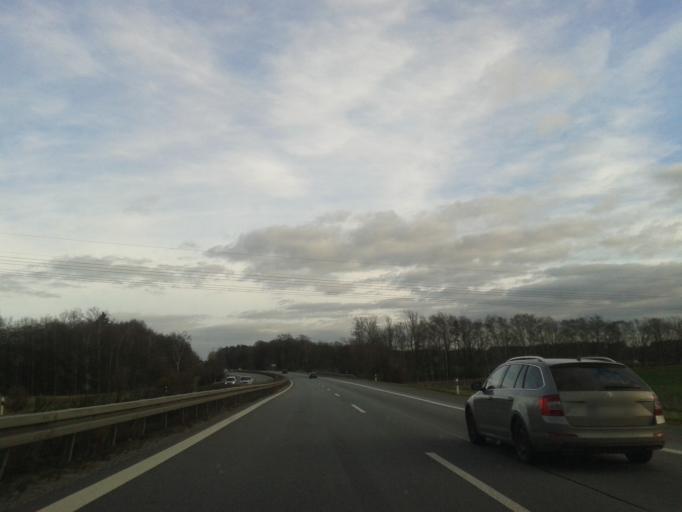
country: DE
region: Saxony
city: Burkau
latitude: 51.1903
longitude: 14.1874
